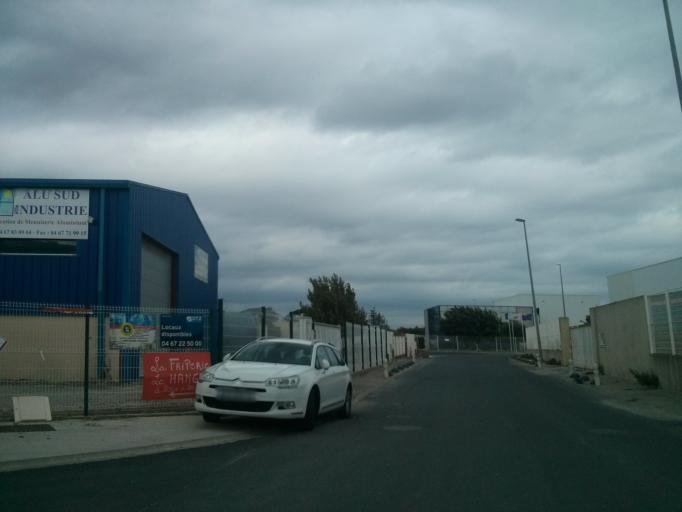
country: FR
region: Languedoc-Roussillon
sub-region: Departement de l'Herault
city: Lunel-Viel
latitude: 43.6798
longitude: 4.1089
